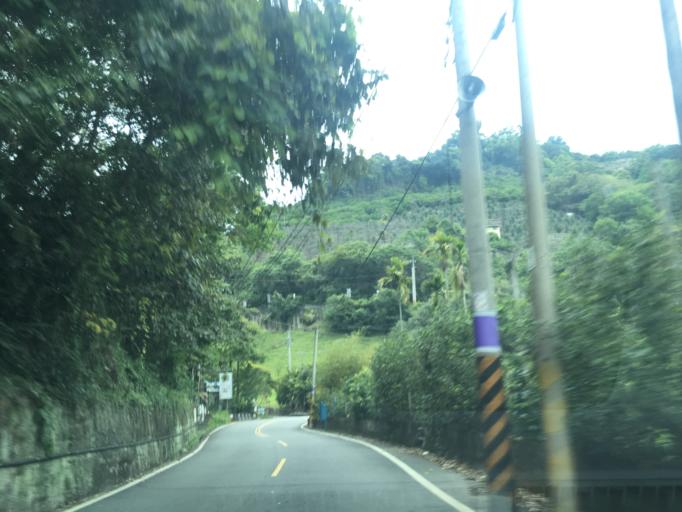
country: TW
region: Taiwan
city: Fengyuan
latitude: 24.1670
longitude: 120.8248
